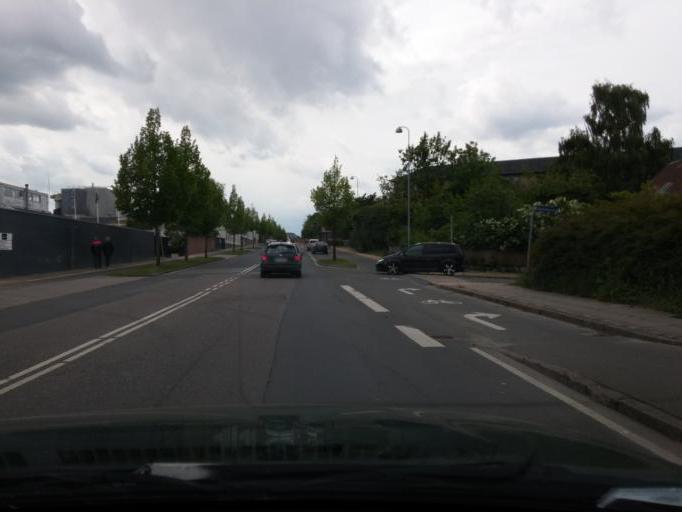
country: DK
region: South Denmark
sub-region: Odense Kommune
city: Odense
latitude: 55.4040
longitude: 10.3733
